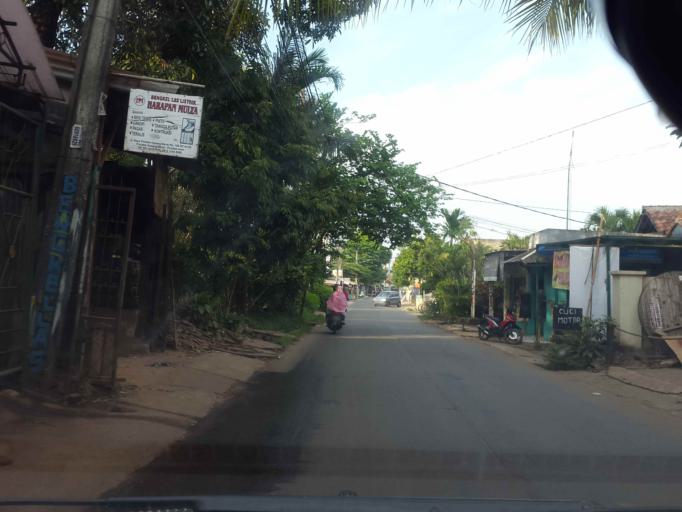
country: ID
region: West Java
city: Ciputat
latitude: -6.2479
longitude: 106.6884
